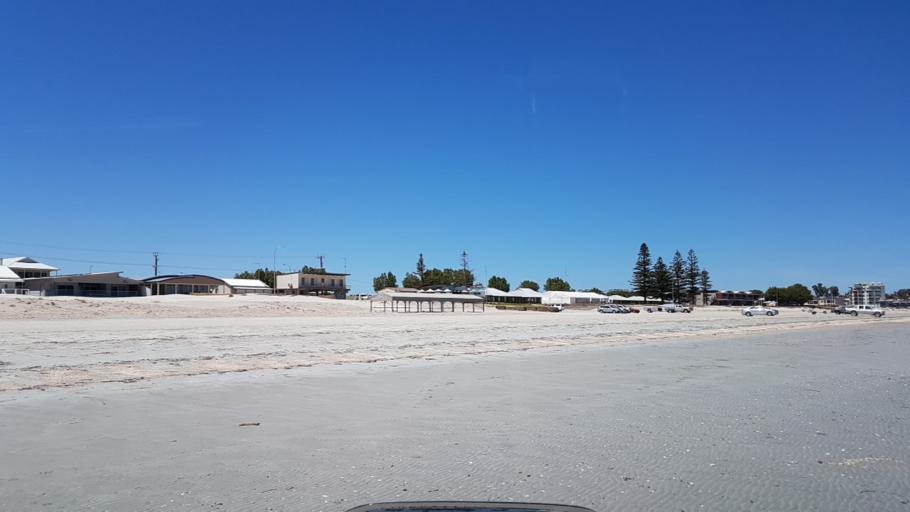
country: AU
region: South Australia
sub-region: Copper Coast
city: Wallaroo
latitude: -33.9172
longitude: 137.6307
